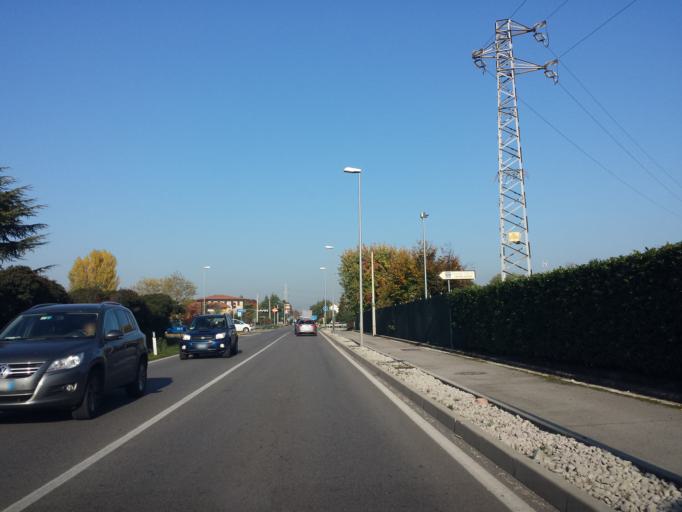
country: IT
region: Veneto
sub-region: Provincia di Treviso
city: Caselle
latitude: 45.7590
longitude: 11.9917
